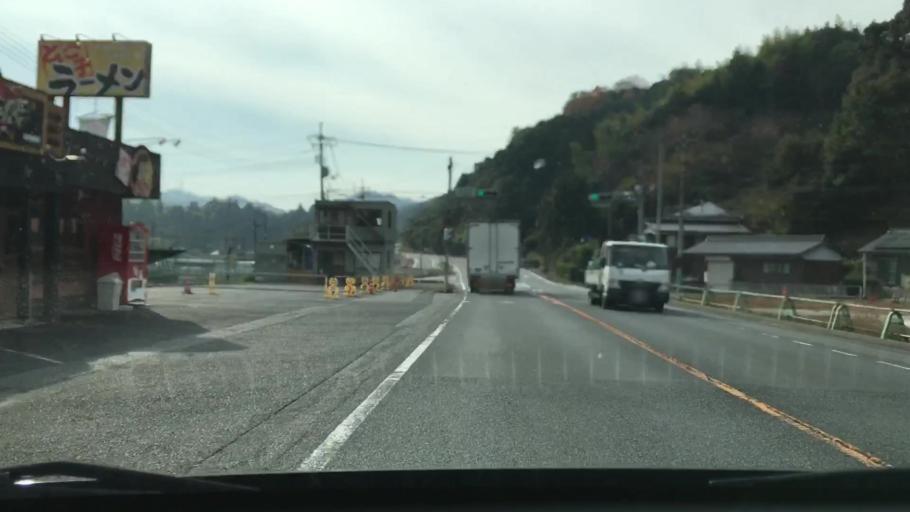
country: JP
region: Yamaguchi
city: Hikari
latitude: 34.0900
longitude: 132.0056
